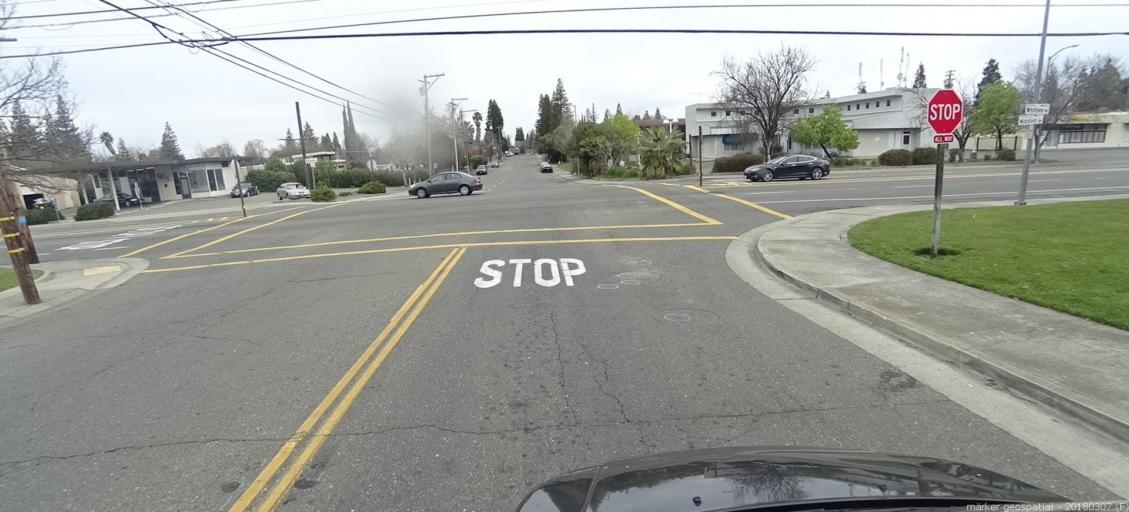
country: US
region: California
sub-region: Sacramento County
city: Carmichael
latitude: 38.6281
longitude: -121.3552
